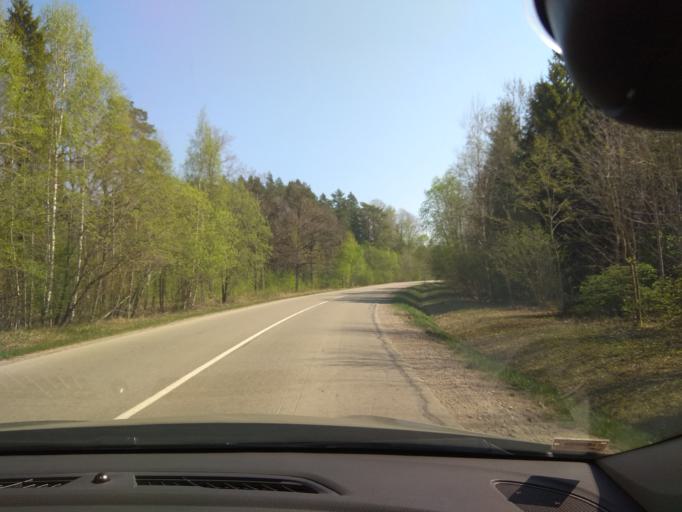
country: LT
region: Panevezys
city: Pasvalys
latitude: 55.9764
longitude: 24.1948
